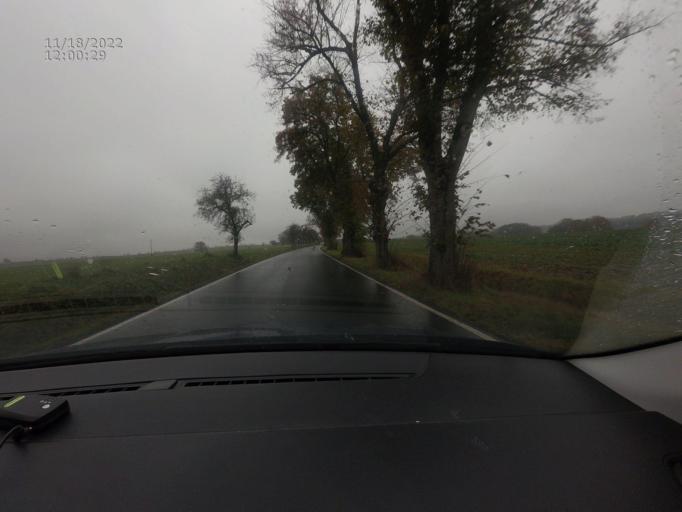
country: CZ
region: Plzensky
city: St'ahlavy
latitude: 49.6658
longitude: 13.4906
